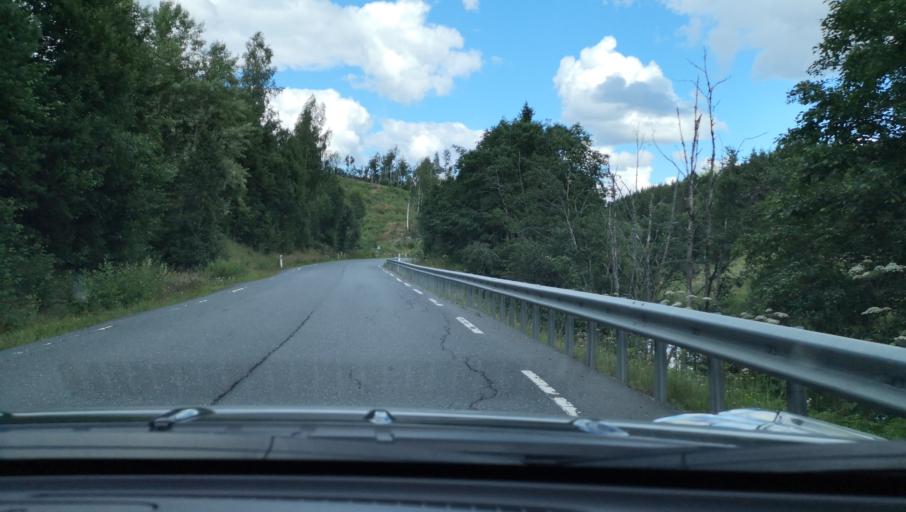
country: NO
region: Ostfold
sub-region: Hobol
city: Tomter
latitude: 59.6451
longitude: 10.9849
